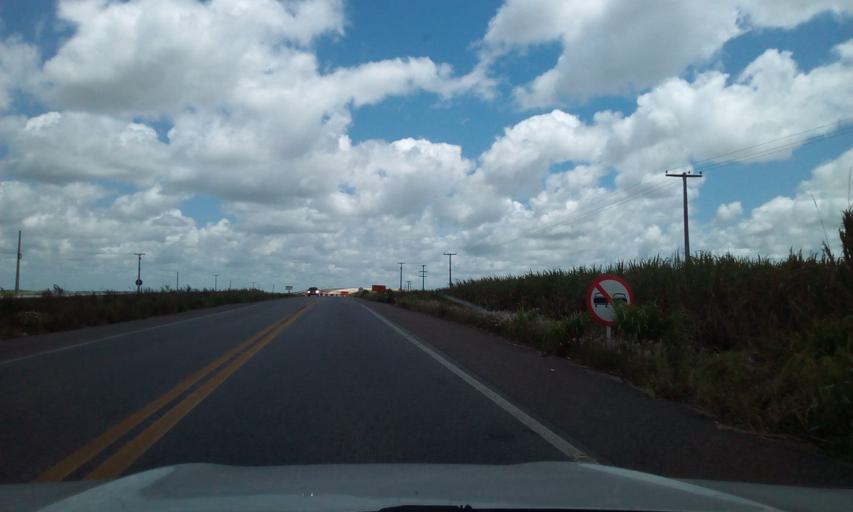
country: BR
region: Alagoas
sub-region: Campo Alegre
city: Campo Alegre
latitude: -9.9010
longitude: -36.3023
